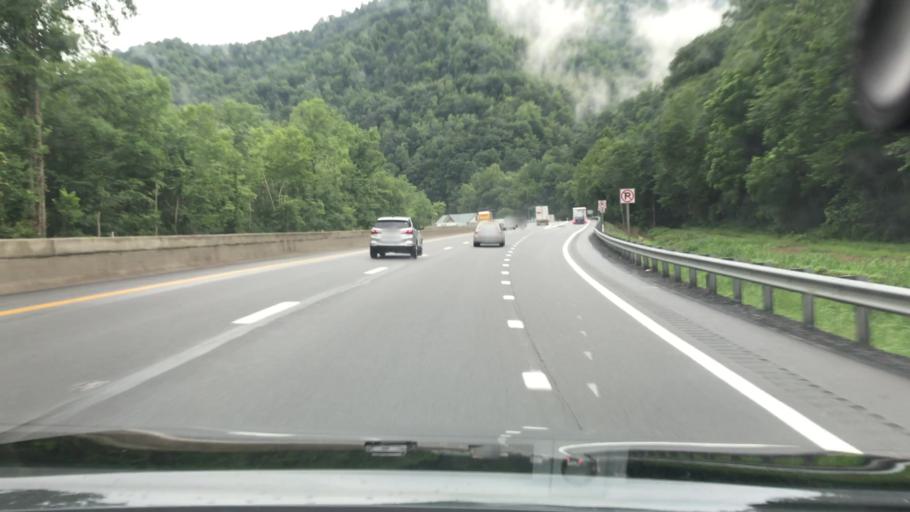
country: US
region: West Virginia
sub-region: Kanawha County
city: Montgomery
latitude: 38.0726
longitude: -81.3799
